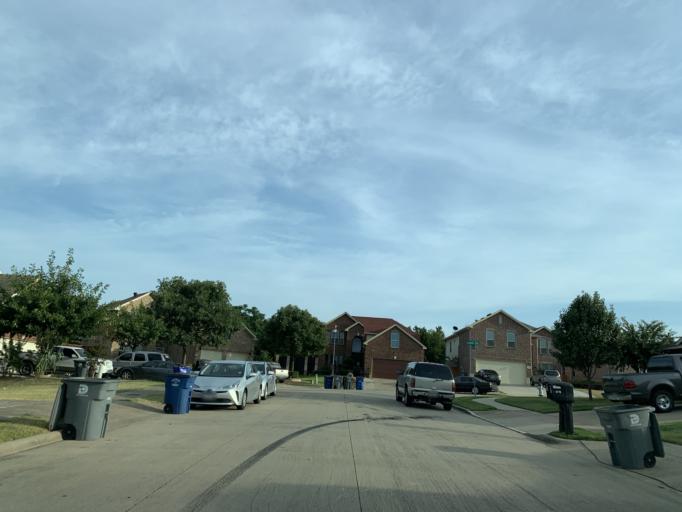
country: US
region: Texas
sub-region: Dallas County
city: Cockrell Hill
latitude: 32.6994
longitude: -96.8923
